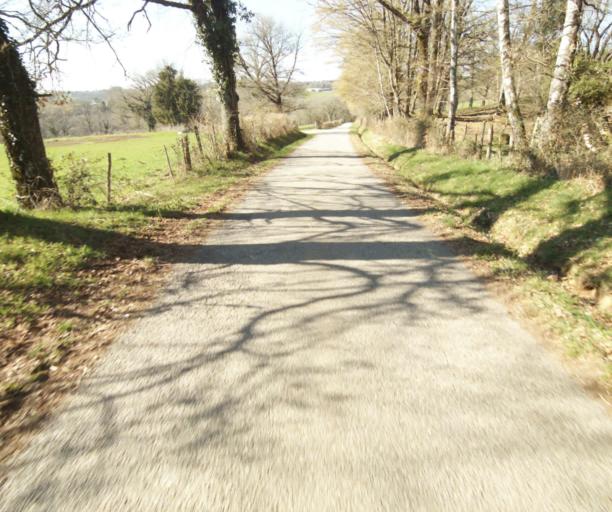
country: FR
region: Limousin
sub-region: Departement de la Correze
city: Chamboulive
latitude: 45.4815
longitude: 1.6871
